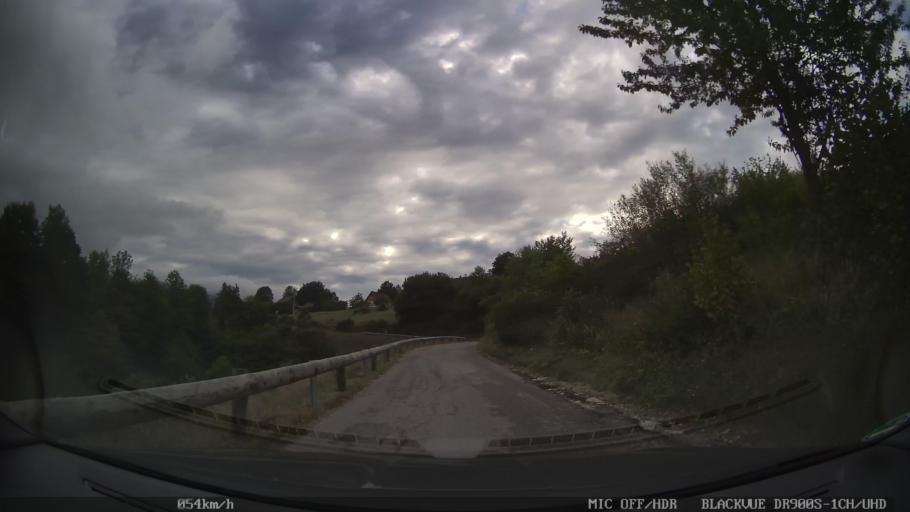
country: HR
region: Licko-Senjska
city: Jezerce
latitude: 44.9246
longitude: 15.5991
